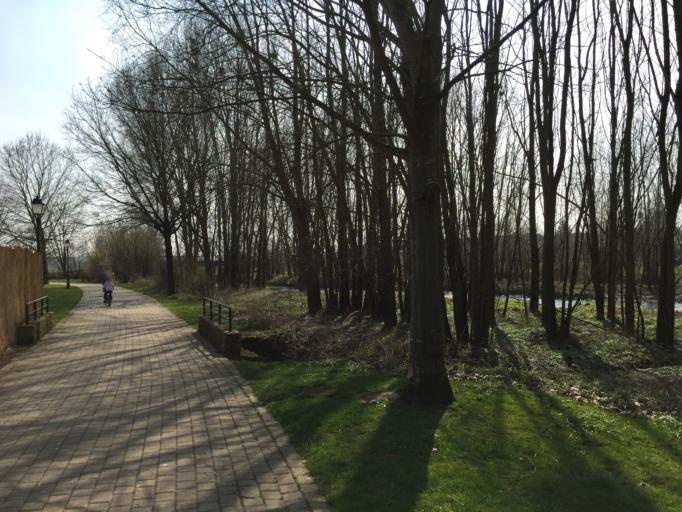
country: LU
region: Luxembourg
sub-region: Canton de Luxembourg
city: Hesperange
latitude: 49.5704
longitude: 6.1575
